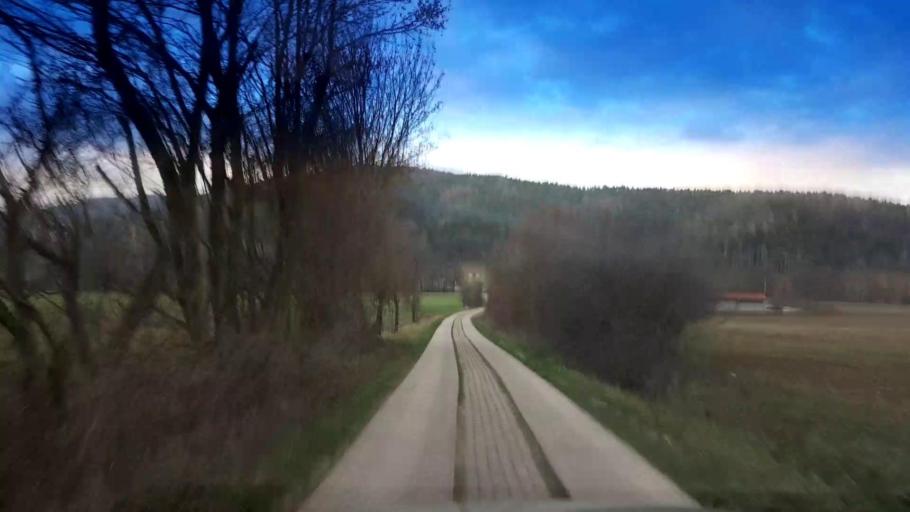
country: DE
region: Bavaria
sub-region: Upper Franconia
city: Schesslitz
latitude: 50.0040
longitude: 11.0712
